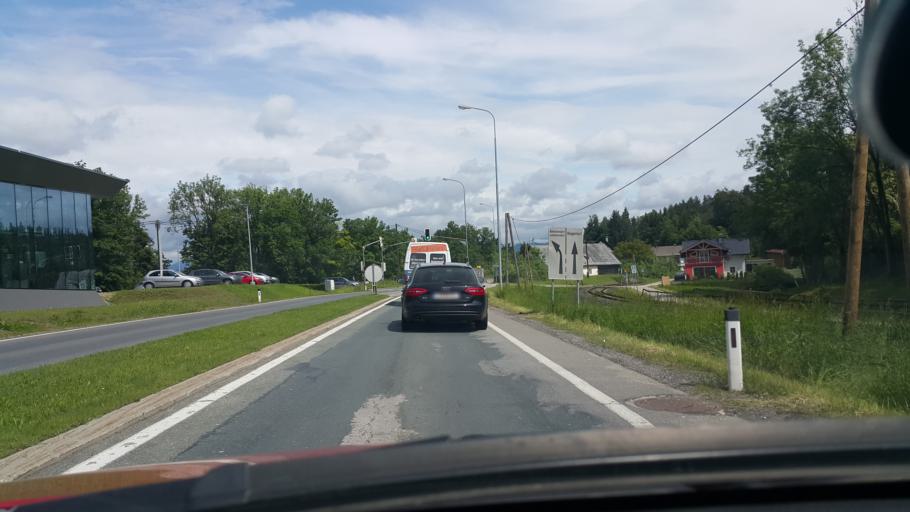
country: AT
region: Carinthia
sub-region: Politischer Bezirk Klagenfurt Land
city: Maria Rain
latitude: 46.5797
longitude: 14.2827
